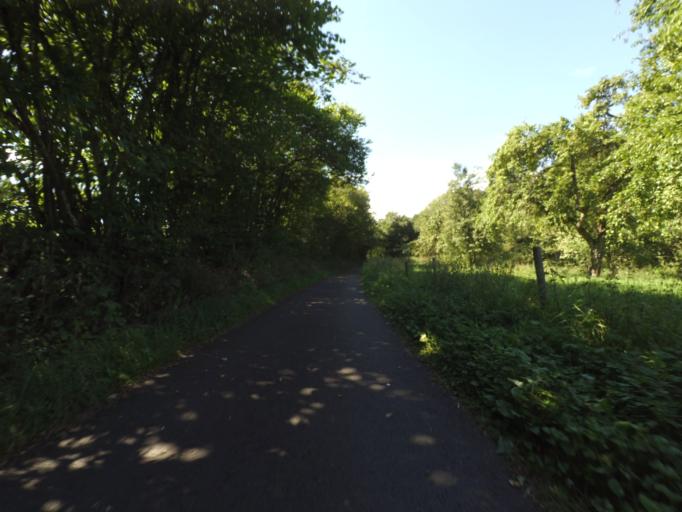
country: DE
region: Rheinland-Pfalz
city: Mehren
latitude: 50.1786
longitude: 6.8652
